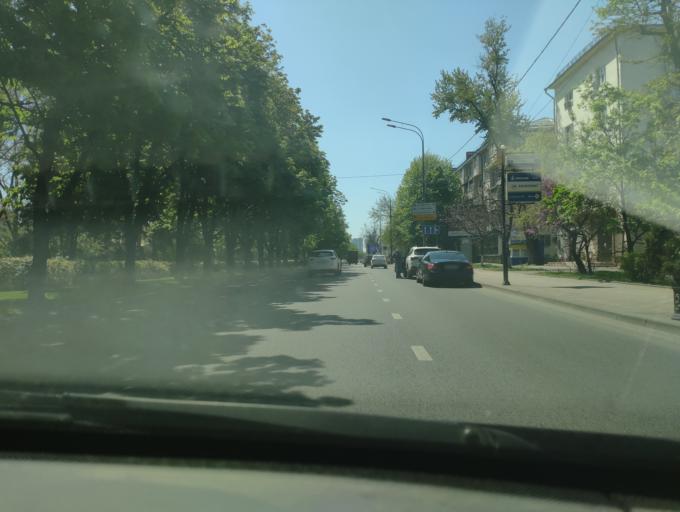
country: RU
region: Krasnodarskiy
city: Krasnodar
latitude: 45.0522
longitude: 38.9797
